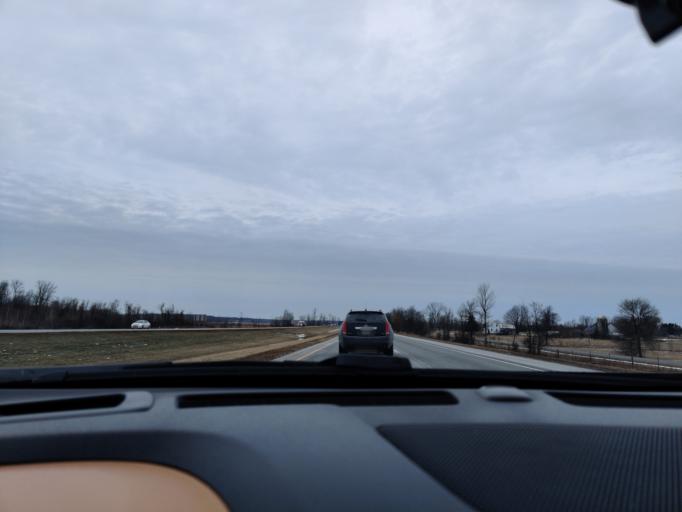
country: US
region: New York
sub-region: St. Lawrence County
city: Norfolk
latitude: 44.9039
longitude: -75.2298
